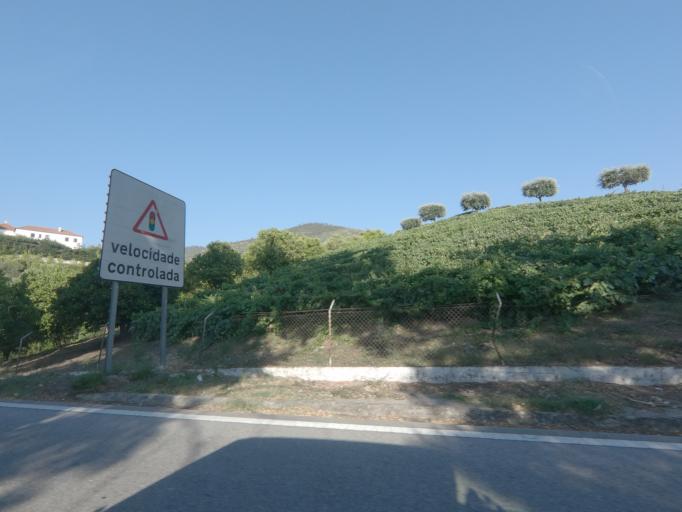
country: PT
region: Viseu
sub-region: Armamar
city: Armamar
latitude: 41.1482
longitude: -7.6859
